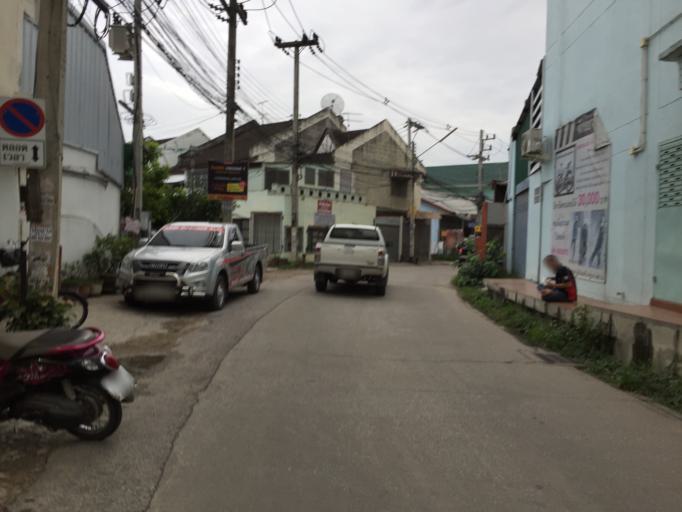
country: TH
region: Chiang Mai
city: Chiang Mai
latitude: 18.8028
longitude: 98.9649
